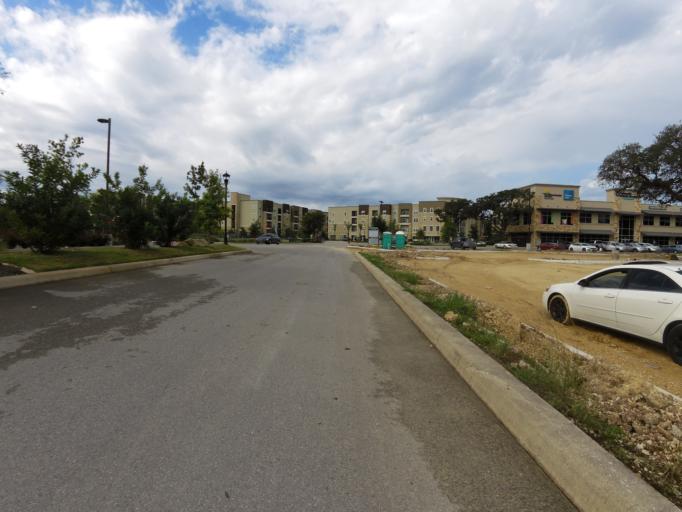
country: US
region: Texas
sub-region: Bexar County
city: Cross Mountain
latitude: 29.6444
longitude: -98.6213
